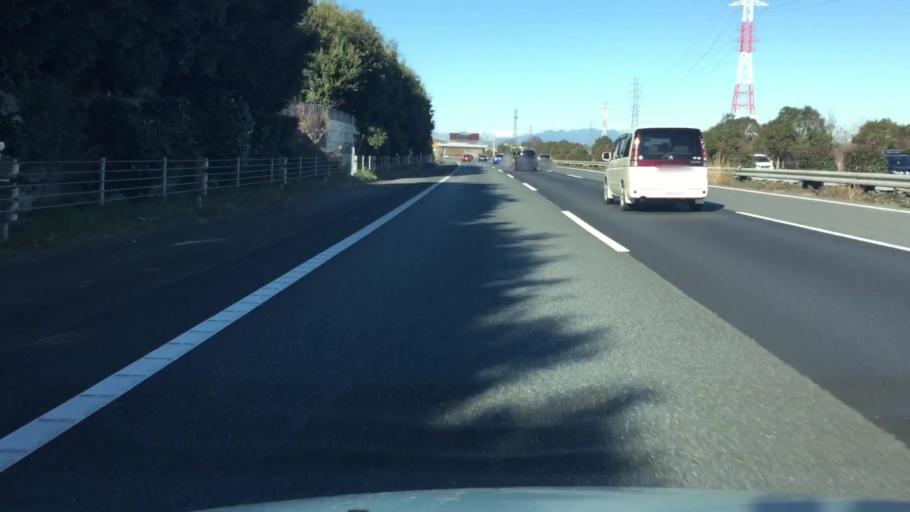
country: JP
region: Saitama
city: Yorii
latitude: 36.1603
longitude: 139.2102
